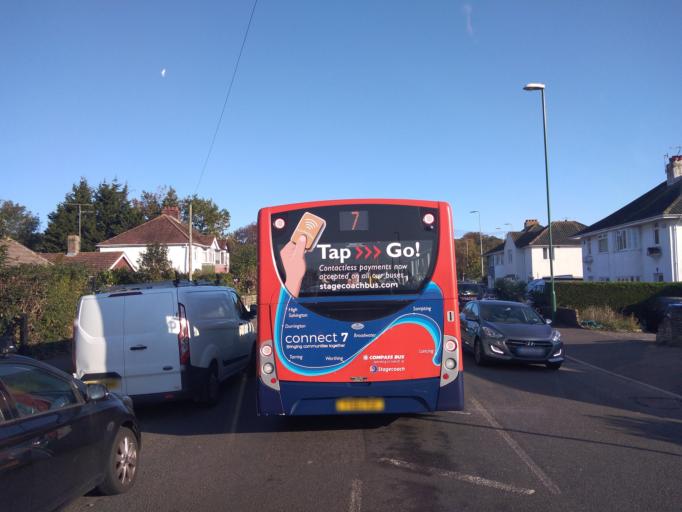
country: GB
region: England
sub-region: West Sussex
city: Lancing
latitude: 50.8359
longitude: -0.3176
